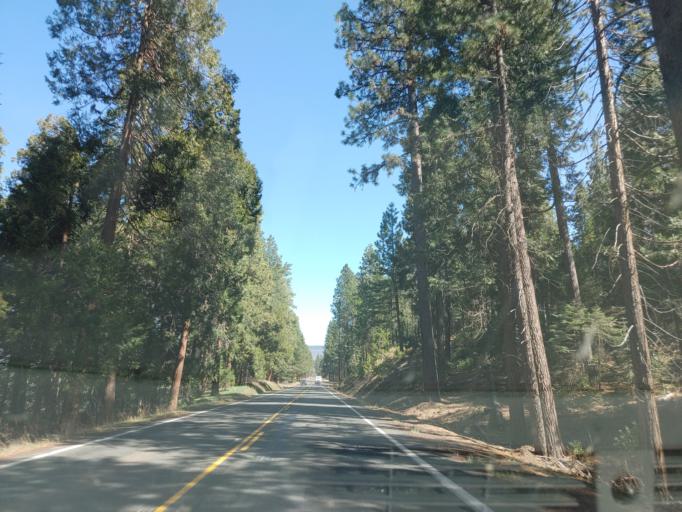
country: US
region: California
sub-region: Shasta County
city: Burney
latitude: 40.7432
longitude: -121.4741
